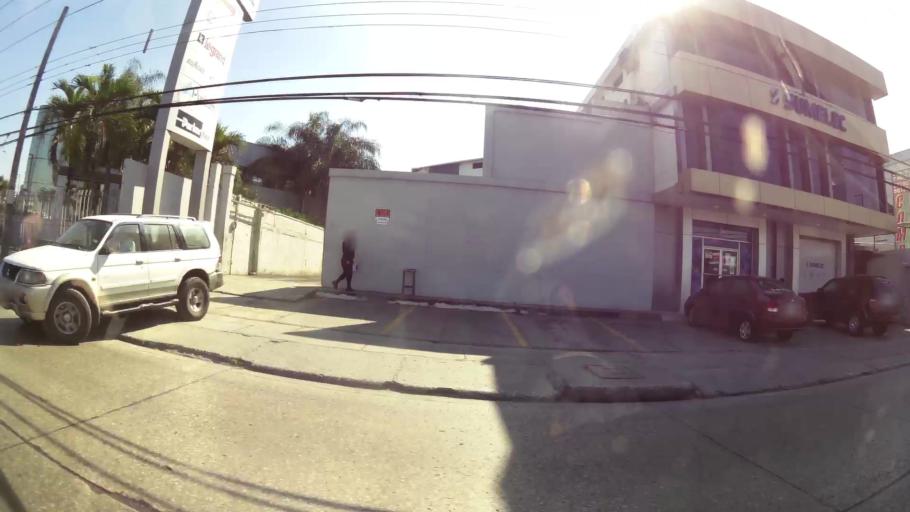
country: EC
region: Guayas
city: Eloy Alfaro
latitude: -2.1485
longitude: -79.9025
